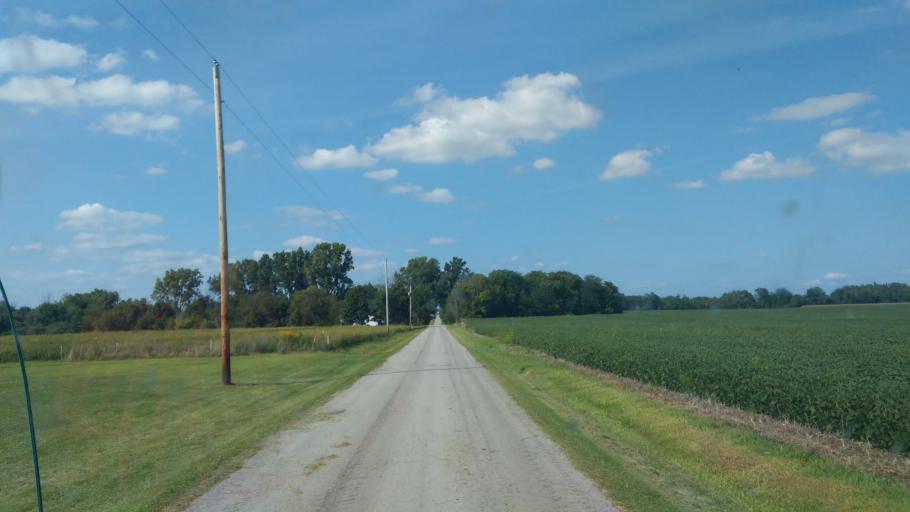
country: US
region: Ohio
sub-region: Hardin County
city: Forest
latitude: 40.7091
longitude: -83.4779
